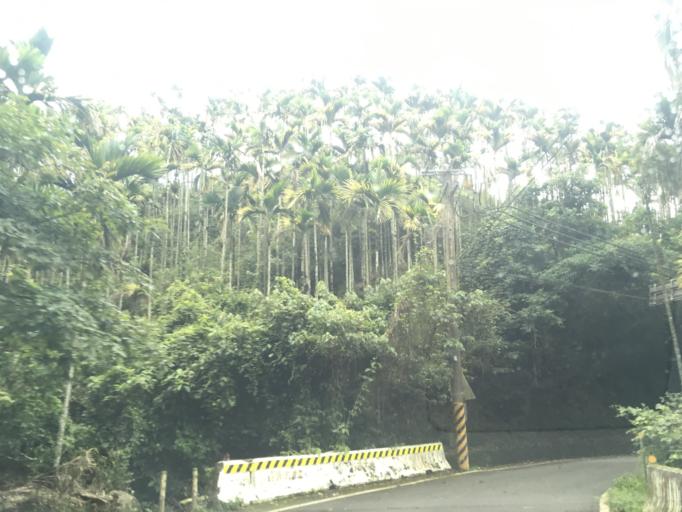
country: TW
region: Taiwan
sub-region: Yunlin
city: Douliu
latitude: 23.5657
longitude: 120.6277
